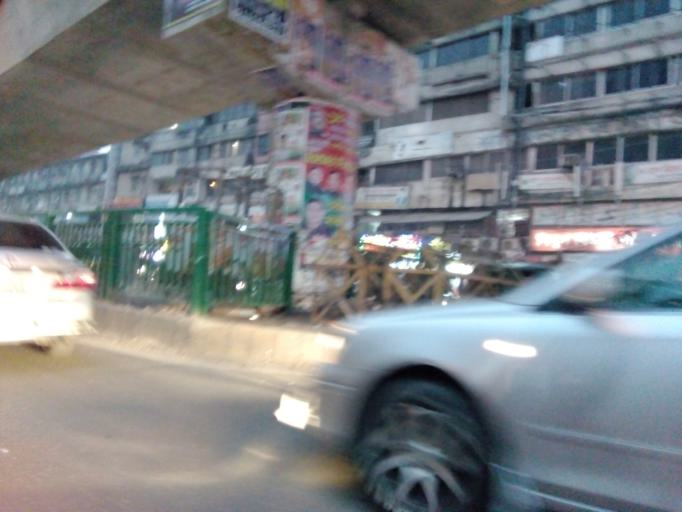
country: BD
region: Dhaka
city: Paltan
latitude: 23.7414
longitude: 90.4118
